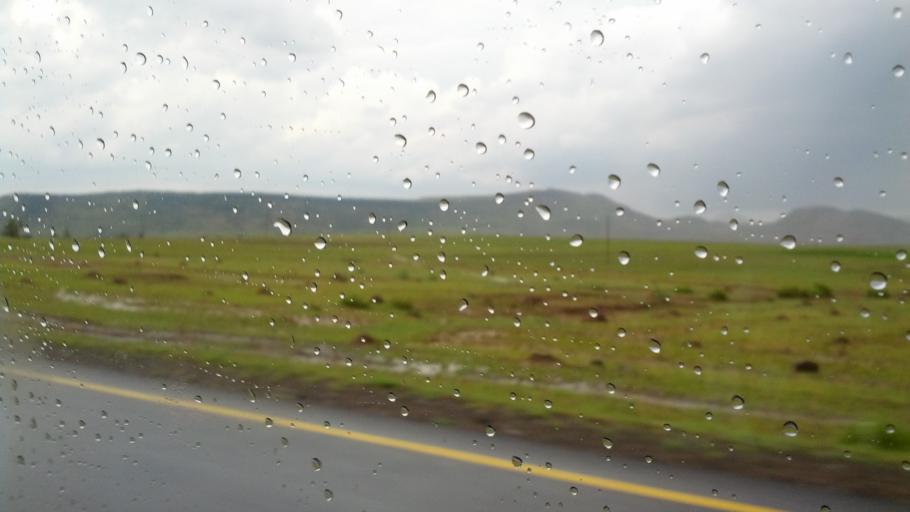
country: LS
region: Mafeteng
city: Mafeteng
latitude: -29.7556
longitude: 27.1227
